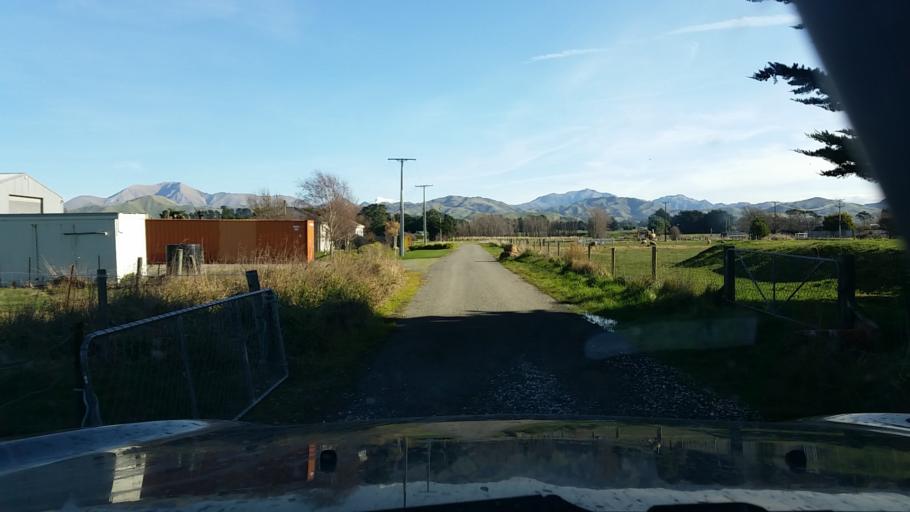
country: NZ
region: Marlborough
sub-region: Marlborough District
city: Blenheim
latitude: -41.8278
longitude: 174.1505
